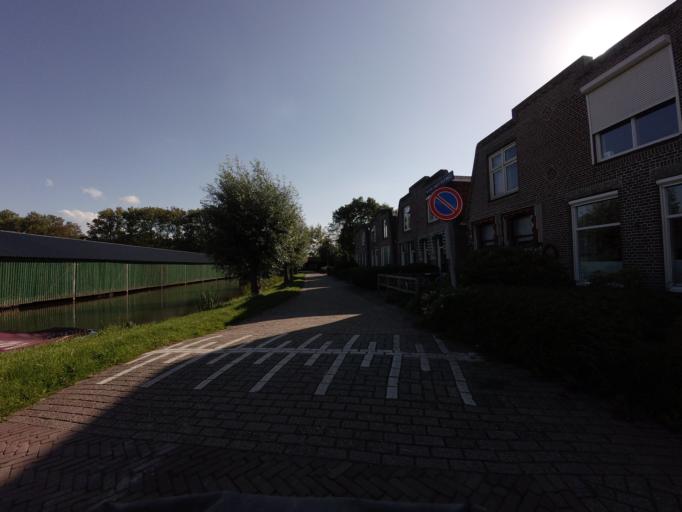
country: NL
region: Friesland
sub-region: Sudwest Fryslan
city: Bolsward
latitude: 53.0595
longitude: 5.5166
